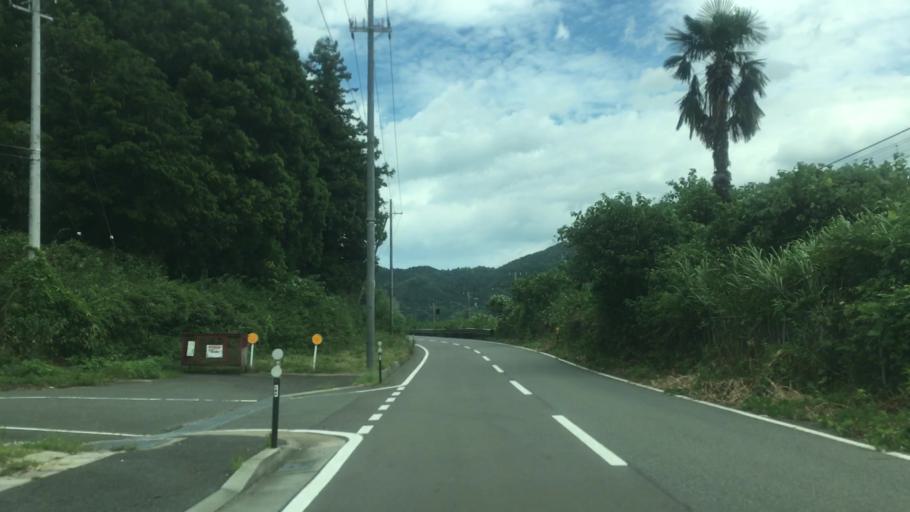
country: JP
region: Hyogo
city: Toyooka
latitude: 35.5715
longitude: 134.8046
